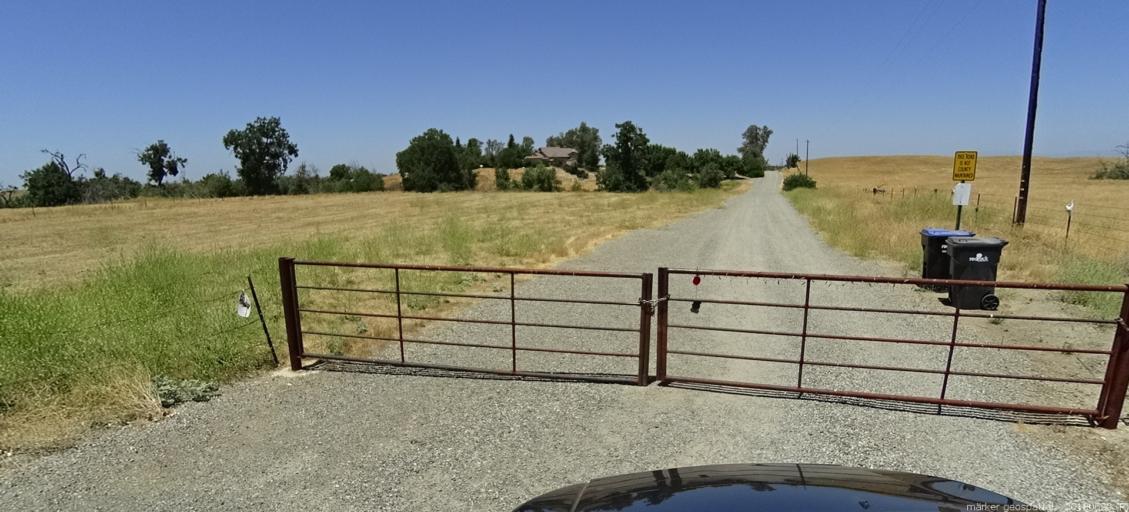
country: US
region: California
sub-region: Madera County
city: Parksdale
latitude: 37.0121
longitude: -119.9653
